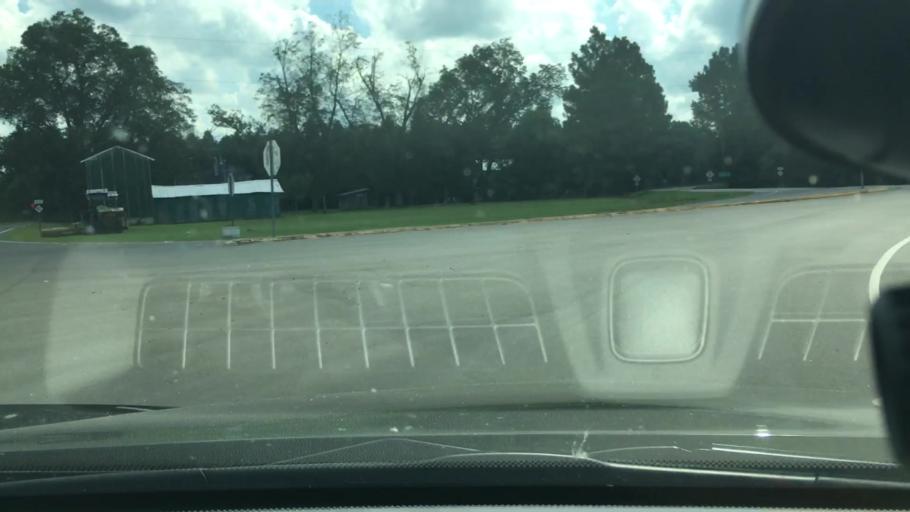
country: US
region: North Carolina
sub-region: Edgecombe County
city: Pinetops
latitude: 35.7790
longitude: -77.5831
